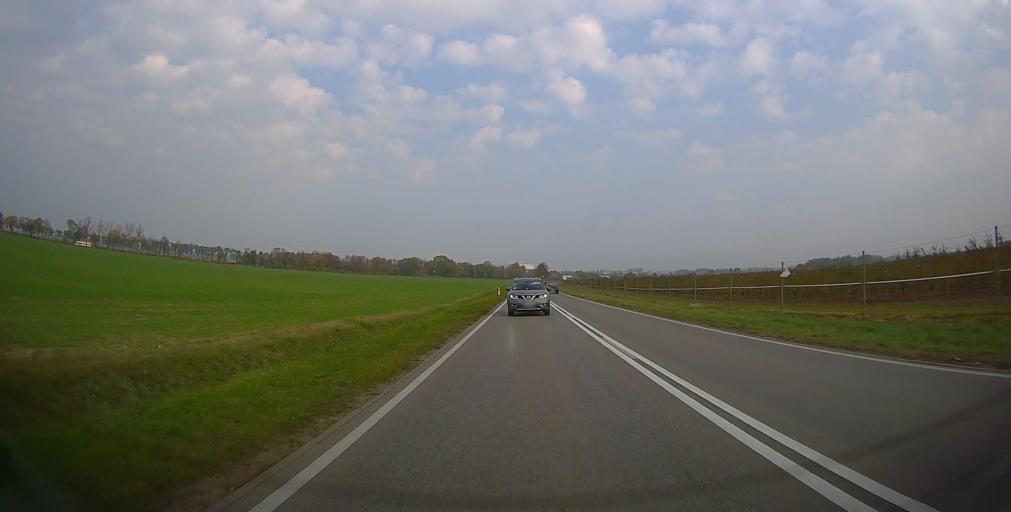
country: PL
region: Masovian Voivodeship
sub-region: Powiat grojecki
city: Belsk Duzy
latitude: 51.8044
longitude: 20.7912
